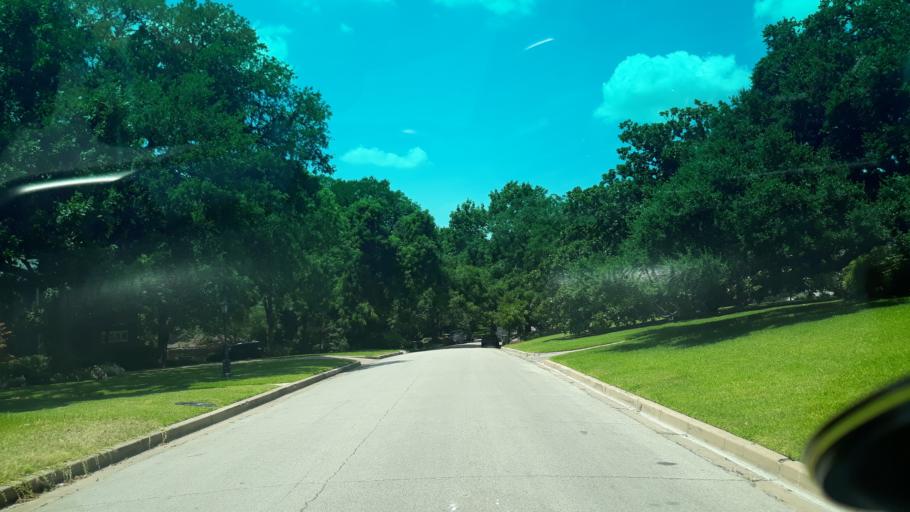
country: US
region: Texas
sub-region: Dallas County
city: Highland Park
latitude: 32.8192
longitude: -96.7379
